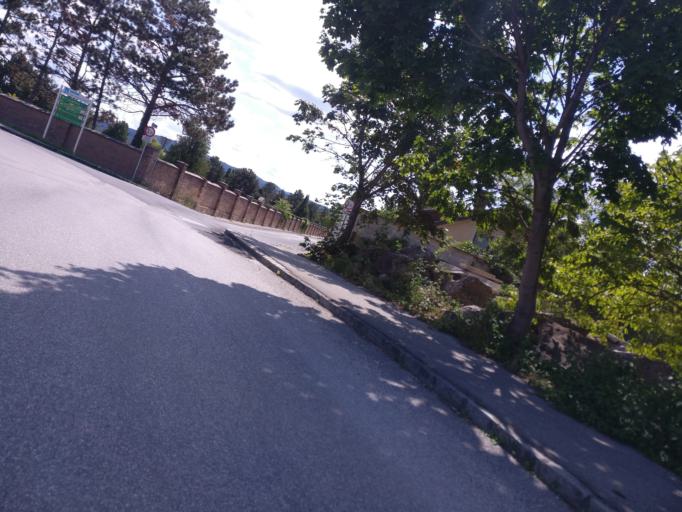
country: AT
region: Lower Austria
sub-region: Politischer Bezirk Neunkirchen
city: Neunkirchen
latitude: 47.7281
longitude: 16.0910
